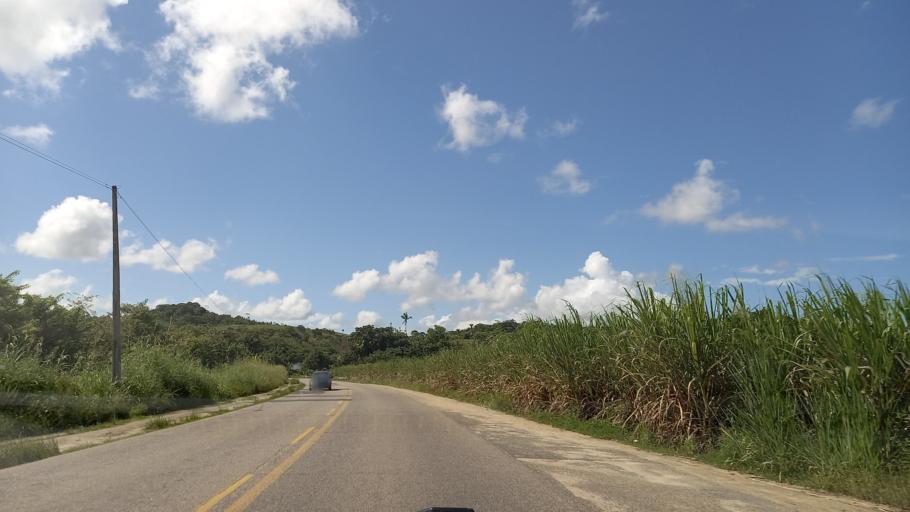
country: BR
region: Pernambuco
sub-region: Barreiros
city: Barreiros
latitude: -8.7766
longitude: -35.1737
